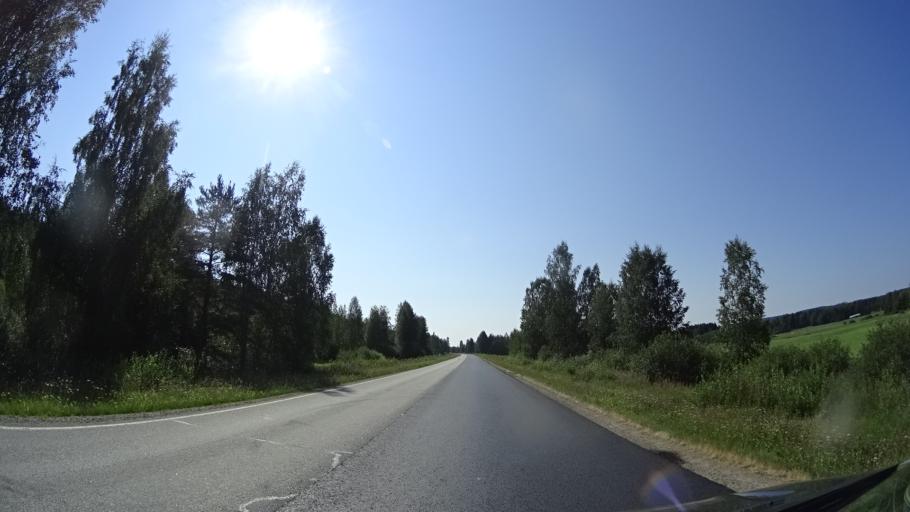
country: FI
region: North Karelia
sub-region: Joensuu
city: Juuka
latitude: 63.2155
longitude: 29.3039
